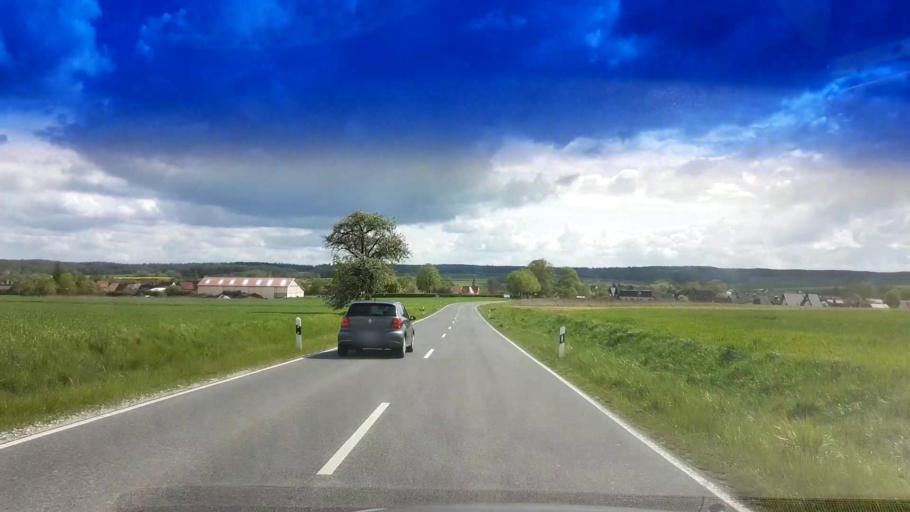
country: DE
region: Bavaria
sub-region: Upper Franconia
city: Frensdorf
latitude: 49.8295
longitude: 10.8414
